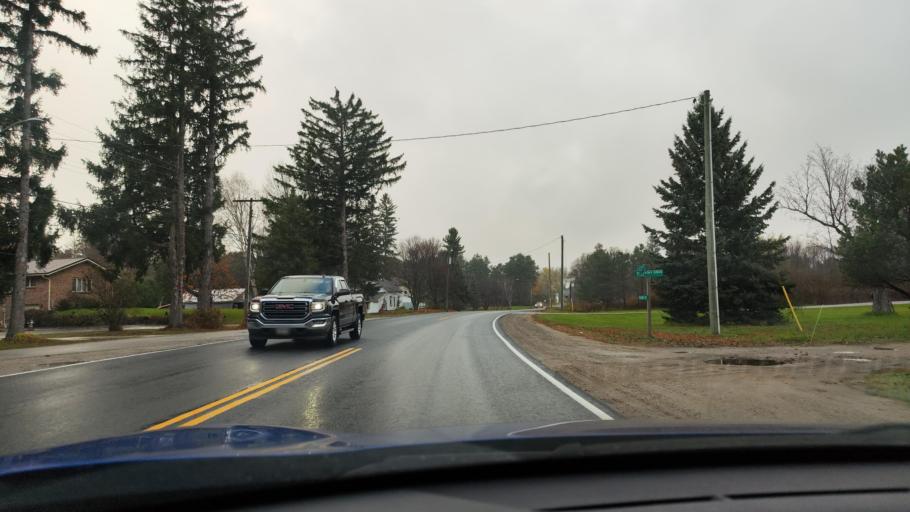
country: CA
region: Ontario
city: Angus
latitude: 44.3404
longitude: -79.9364
